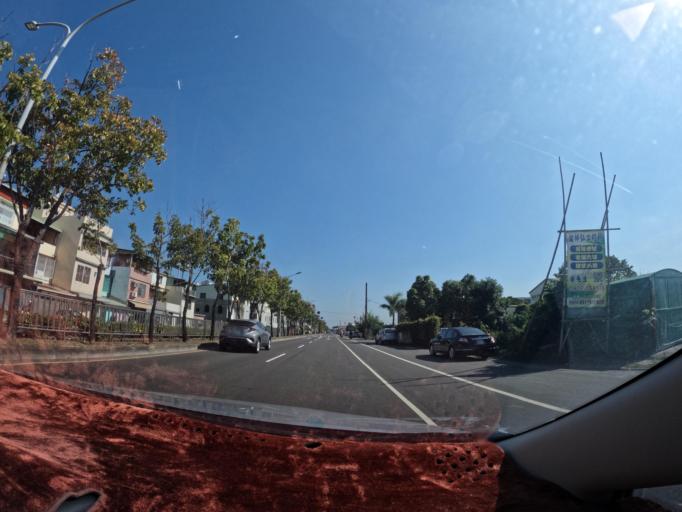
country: TW
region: Taiwan
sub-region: Tainan
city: Tainan
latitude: 22.9994
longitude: 120.2637
